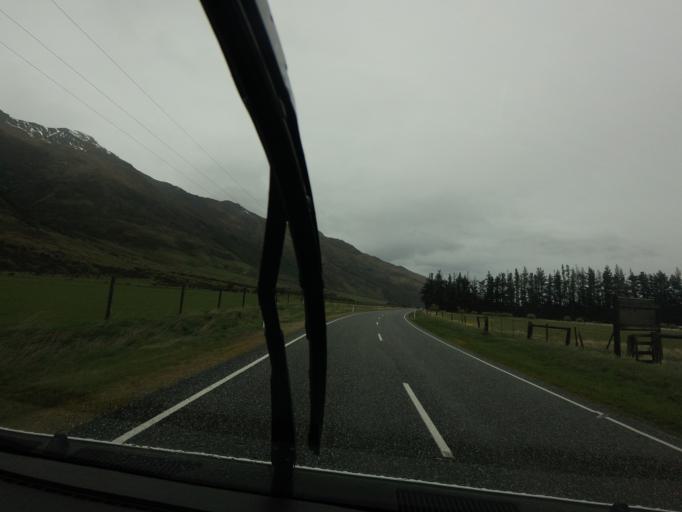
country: NZ
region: Otago
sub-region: Queenstown-Lakes District
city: Wanaka
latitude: -44.2740
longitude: 169.2015
